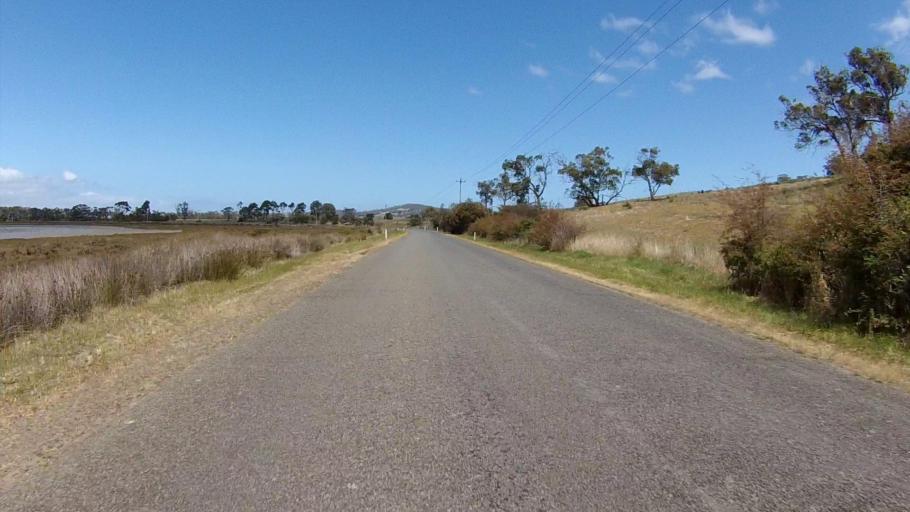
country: AU
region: Tasmania
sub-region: Clarence
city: Lauderdale
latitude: -42.9264
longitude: 147.4821
